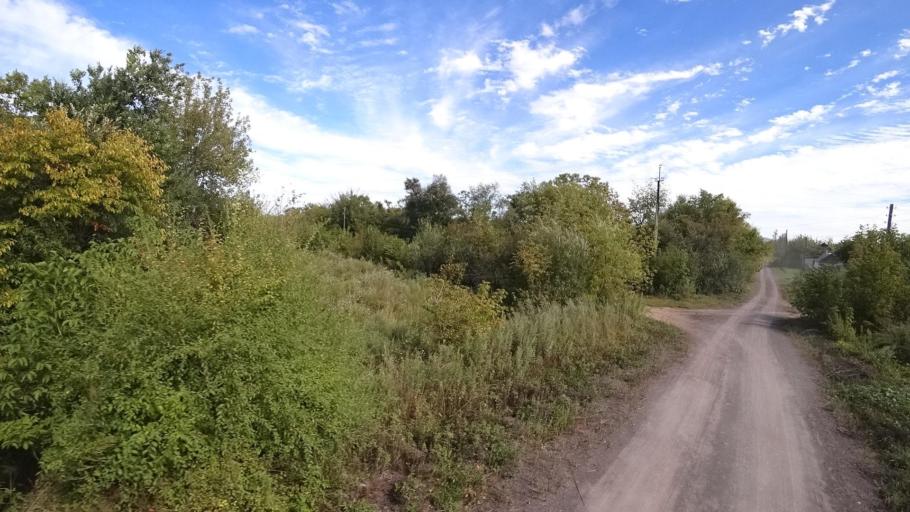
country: RU
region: Primorskiy
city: Yakovlevka
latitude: 44.4335
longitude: 133.5679
